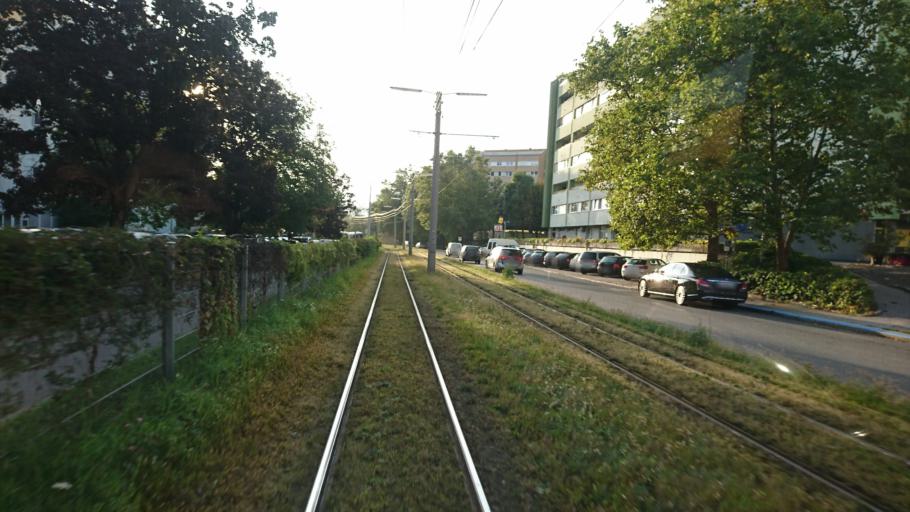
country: AT
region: Upper Austria
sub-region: Linz Stadt
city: Linz
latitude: 48.3322
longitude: 14.3104
